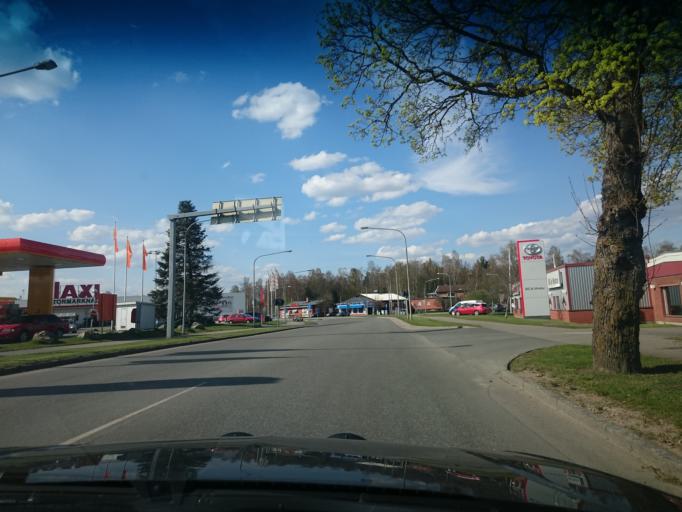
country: SE
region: Joenkoeping
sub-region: Vetlanda Kommun
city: Vetlanda
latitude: 57.4246
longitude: 15.0978
